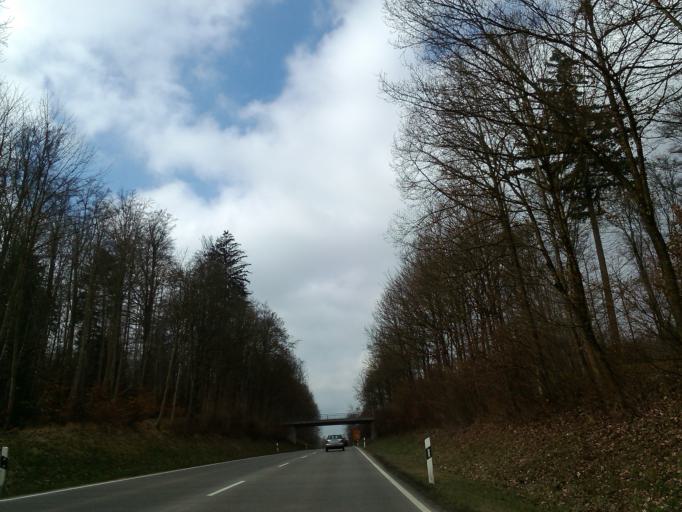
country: DE
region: Bavaria
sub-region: Swabia
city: Krumbach
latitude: 48.2454
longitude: 10.3991
